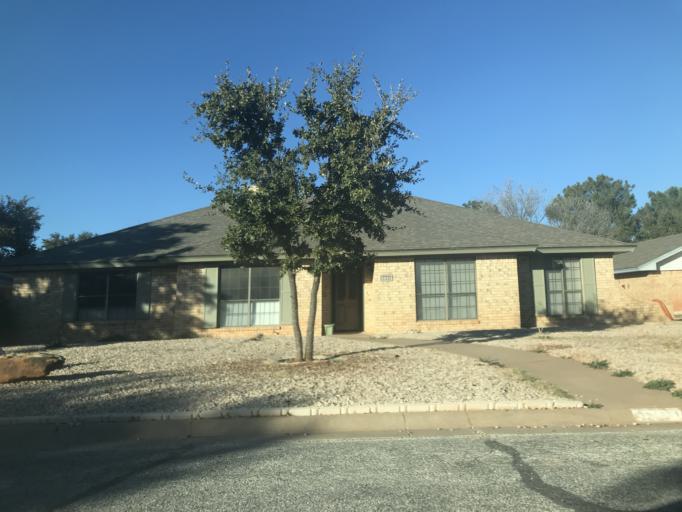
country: US
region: Texas
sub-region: Tom Green County
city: San Angelo
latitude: 31.4263
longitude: -100.4945
